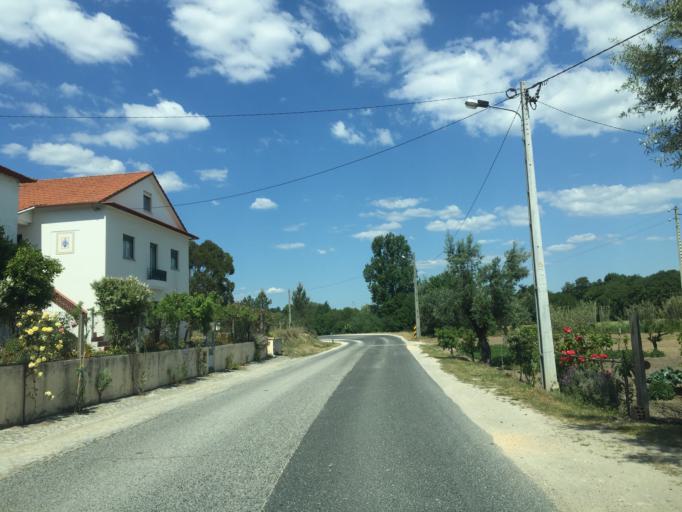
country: PT
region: Santarem
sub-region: Ourem
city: Ourem
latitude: 39.7197
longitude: -8.5179
